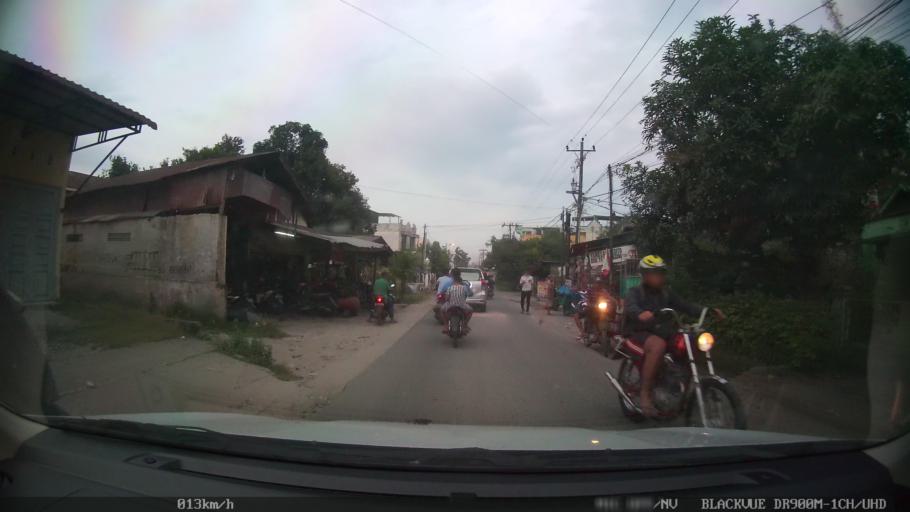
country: ID
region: North Sumatra
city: Sunggal
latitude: 3.5856
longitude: 98.5942
